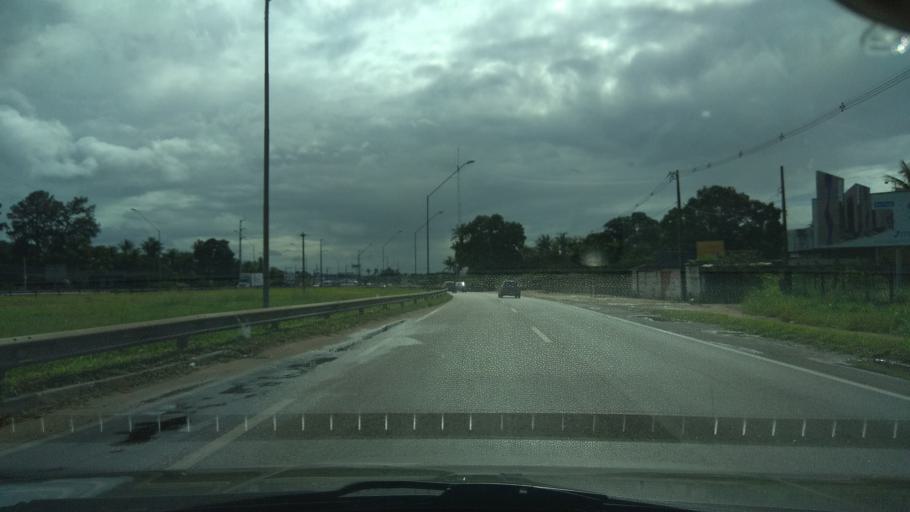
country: BR
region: Bahia
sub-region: Conceicao Do Jacuipe
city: Conceicao do Jacuipe
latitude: -12.3190
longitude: -38.8732
